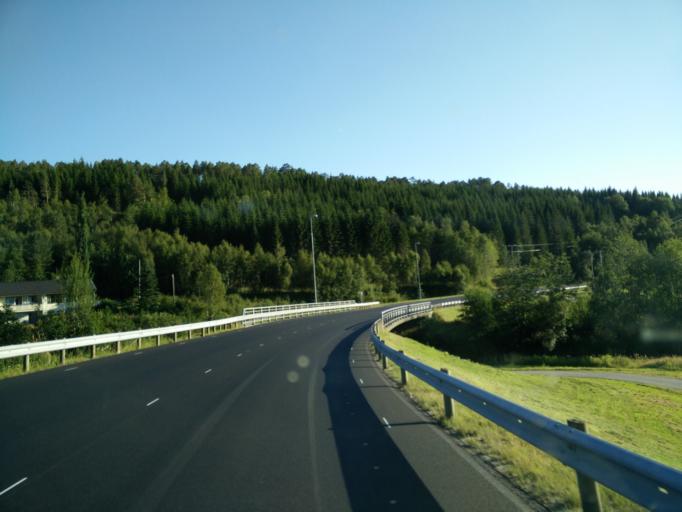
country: NO
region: More og Romsdal
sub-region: Halsa
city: Liaboen
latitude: 63.0853
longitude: 8.3492
